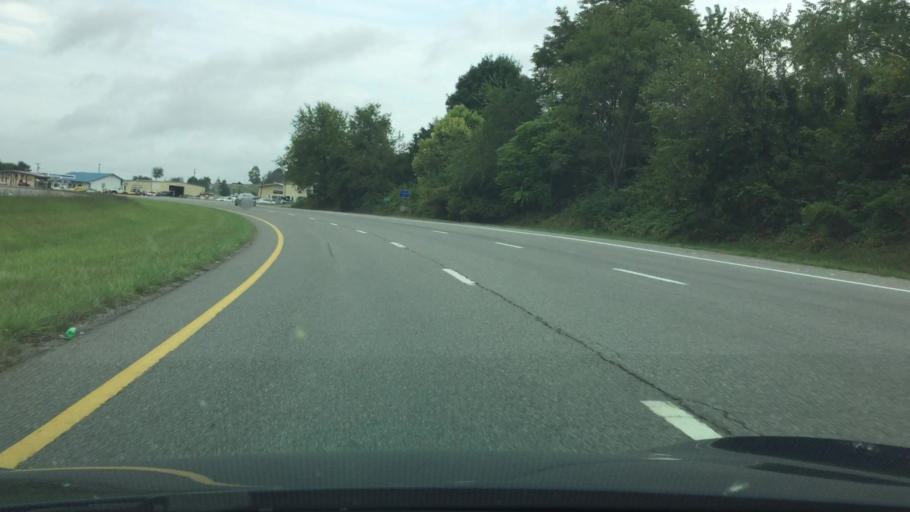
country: US
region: Virginia
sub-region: City of Radford
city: Radford
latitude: 37.0986
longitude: -80.5084
